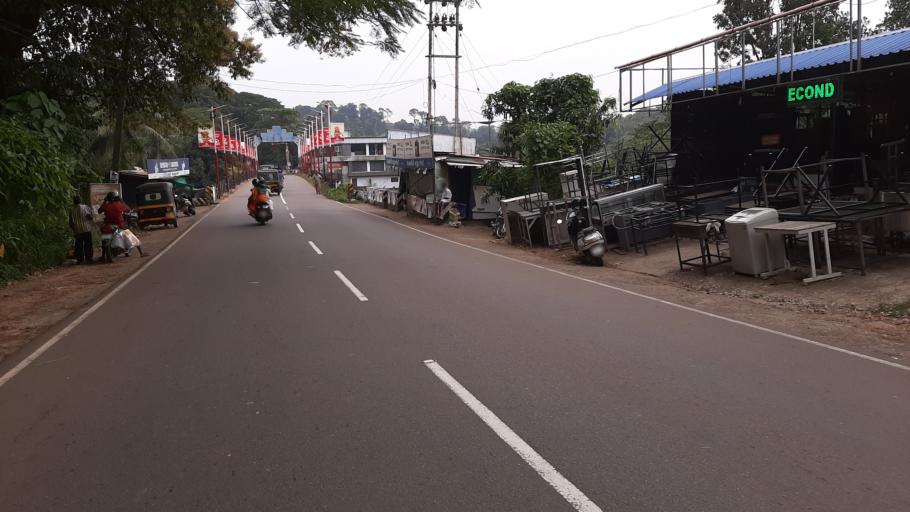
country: IN
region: Kerala
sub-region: Kottayam
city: Erattupetta
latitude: 9.4963
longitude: 76.8489
